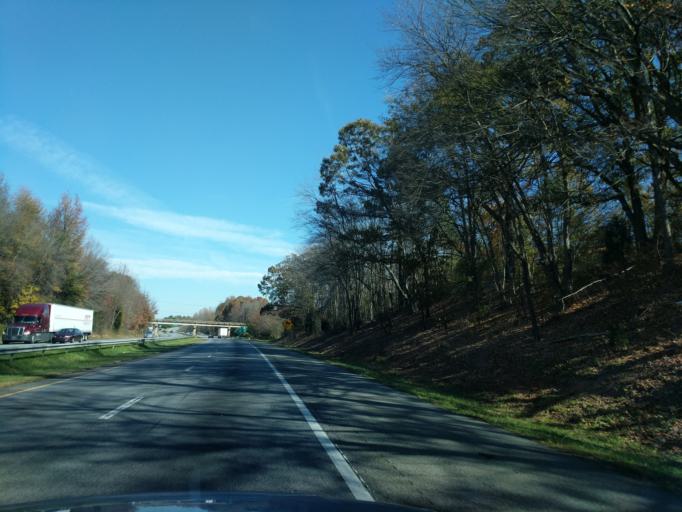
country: US
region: North Carolina
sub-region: Cleveland County
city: Kings Mountain
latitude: 35.2345
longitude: -81.3172
